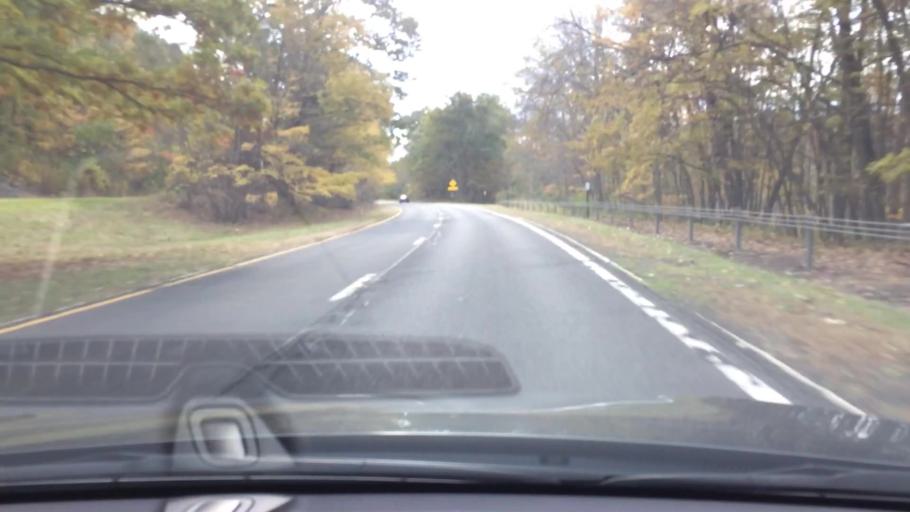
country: US
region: New York
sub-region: Dutchess County
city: Pleasant Valley
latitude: 41.7176
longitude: -73.7843
